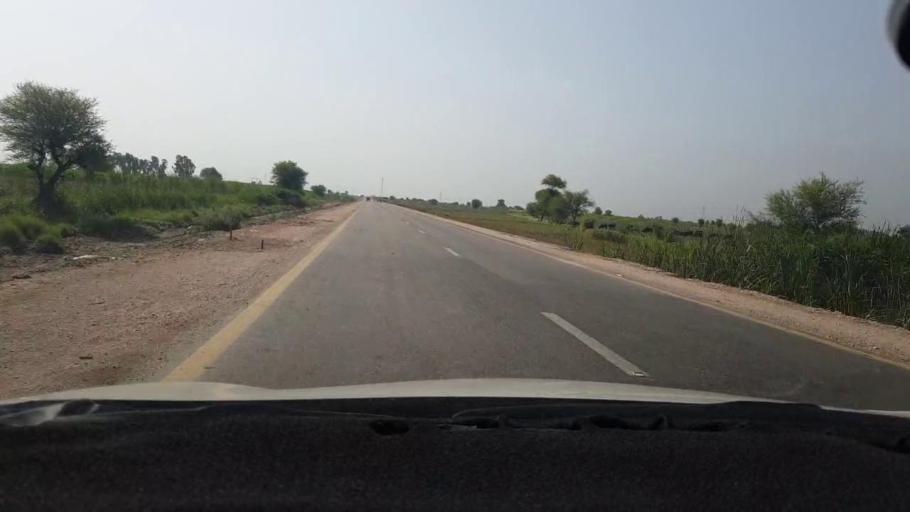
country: PK
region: Sindh
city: Jhol
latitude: 25.8424
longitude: 69.0618
